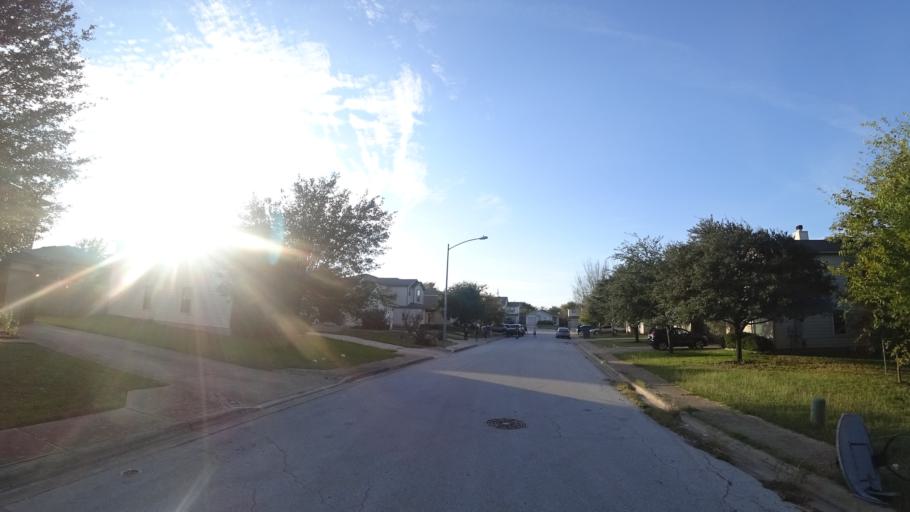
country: US
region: Texas
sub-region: Travis County
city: Pflugerville
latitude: 30.4137
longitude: -97.6502
